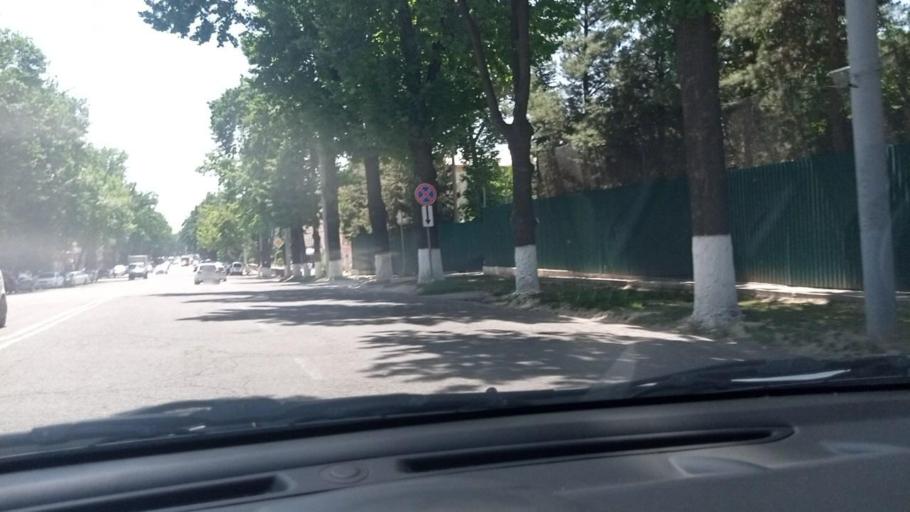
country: UZ
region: Toshkent Shahri
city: Tashkent
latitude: 41.2867
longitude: 69.2276
